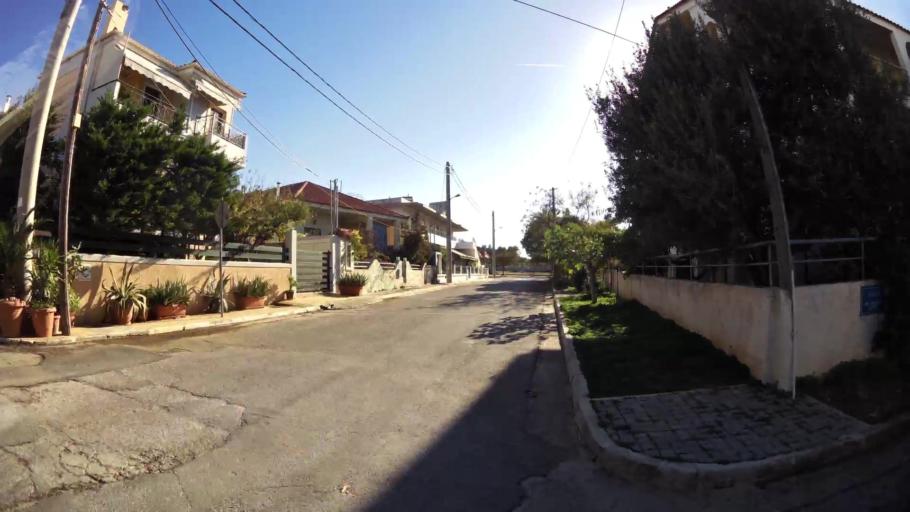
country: GR
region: Attica
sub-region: Nomarchia Anatolikis Attikis
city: Kalyvia Thorikou
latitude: 37.8362
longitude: 23.9245
